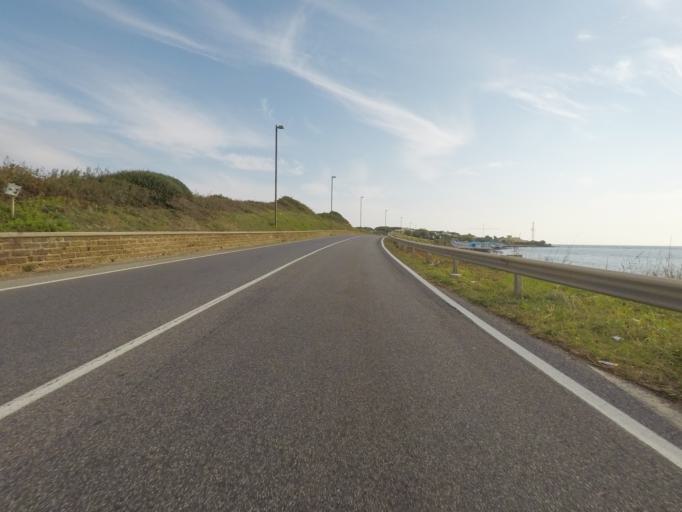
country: IT
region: Latium
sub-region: Citta metropolitana di Roma Capitale
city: Santa Marinella
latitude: 42.0378
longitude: 11.8325
